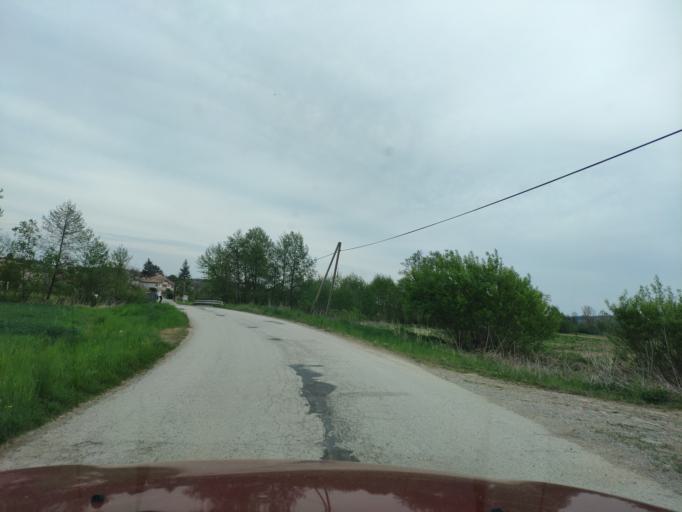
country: SK
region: Banskobystricky
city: Revuca
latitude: 48.5022
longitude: 20.1958
